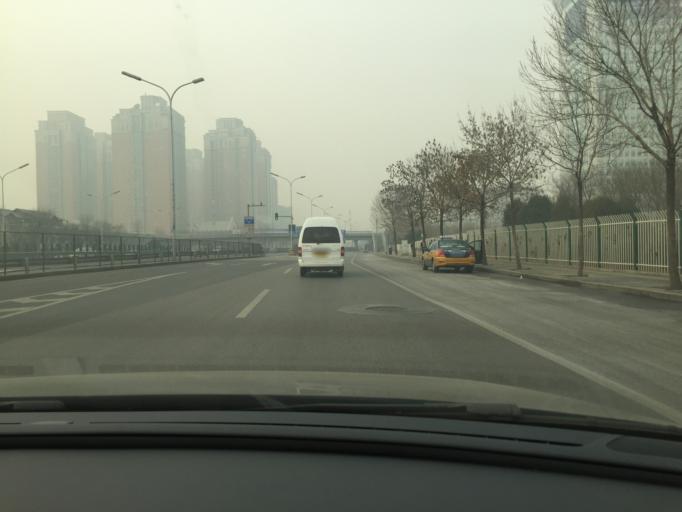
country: CN
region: Beijing
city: Datun
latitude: 39.9869
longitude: 116.3844
